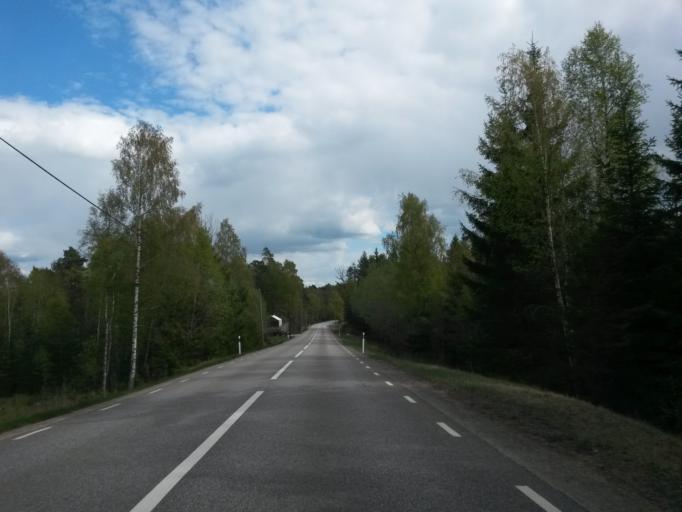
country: SE
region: Vaestra Goetaland
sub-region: Vargarda Kommun
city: Vargarda
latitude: 57.9147
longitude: 12.8920
